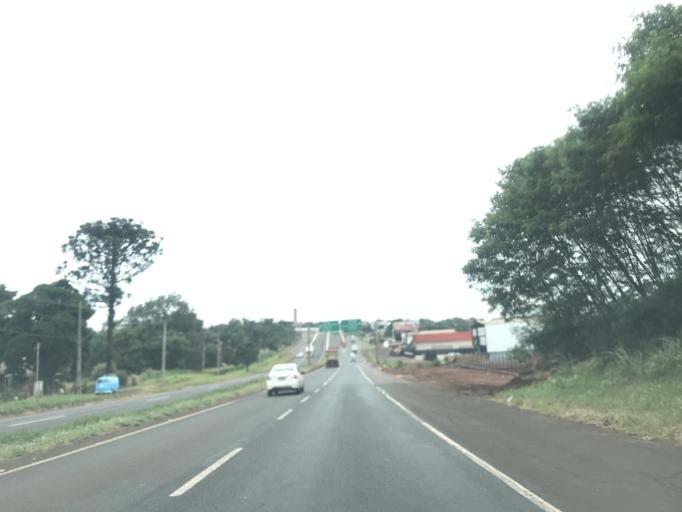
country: BR
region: Parana
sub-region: Maringa
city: Maringa
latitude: -23.4060
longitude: -51.9928
